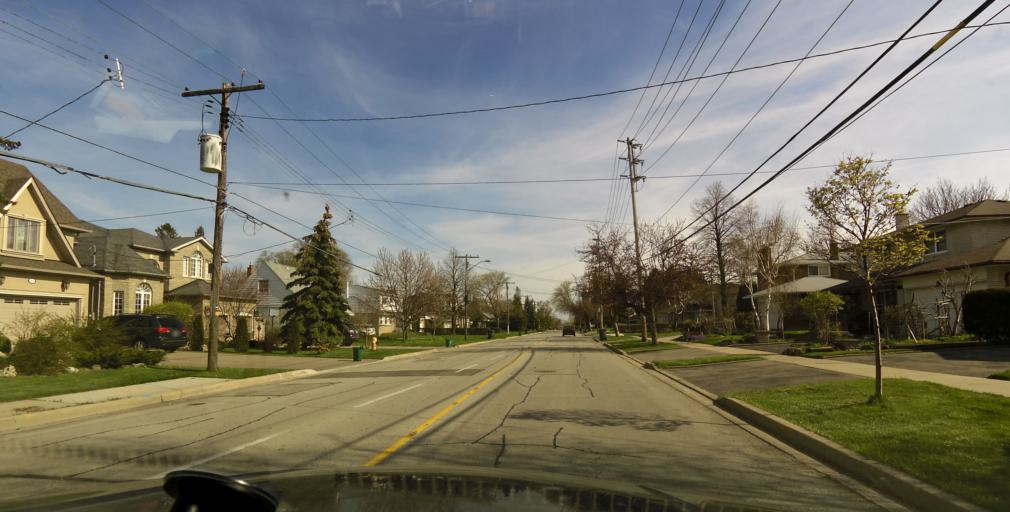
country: CA
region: Ontario
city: Etobicoke
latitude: 43.6340
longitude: -79.5671
